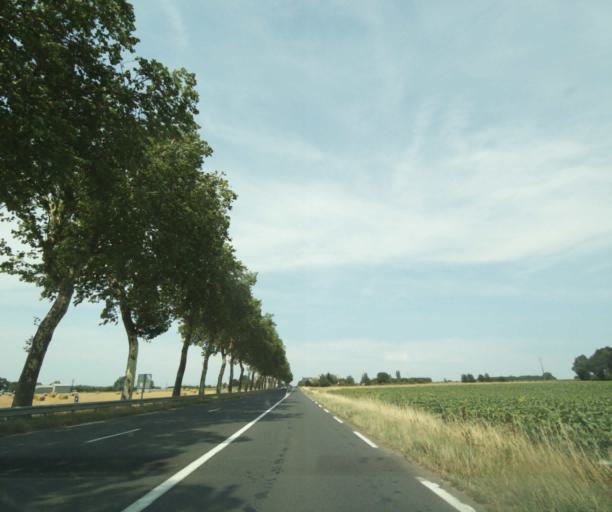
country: FR
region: Centre
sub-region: Departement d'Indre-et-Loire
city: Sainte-Maure-de-Touraine
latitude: 47.1289
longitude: 0.6308
